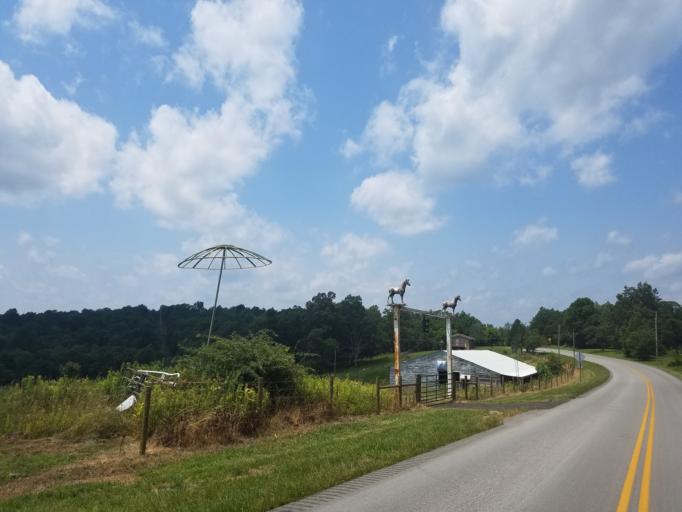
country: US
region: Kentucky
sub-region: Hart County
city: Munfordville
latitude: 37.3119
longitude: -86.0733
